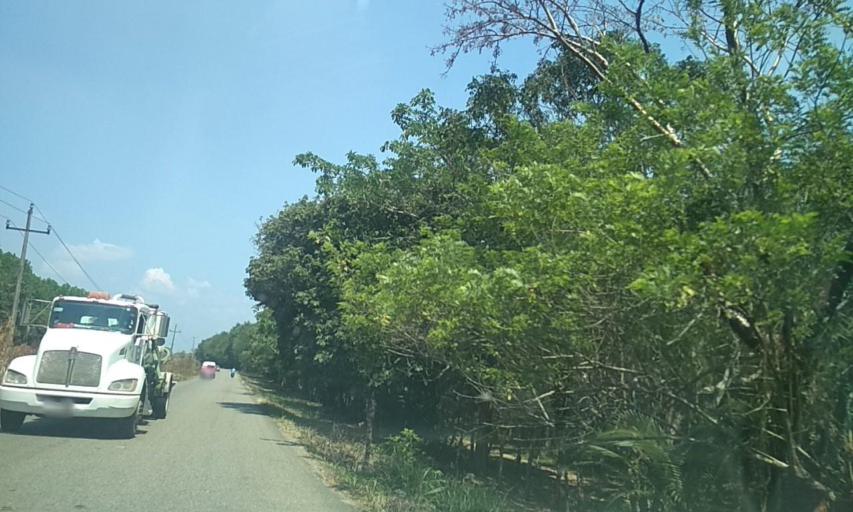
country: MX
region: Tabasco
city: Huimanguillo
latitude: 17.7999
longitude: -93.4692
